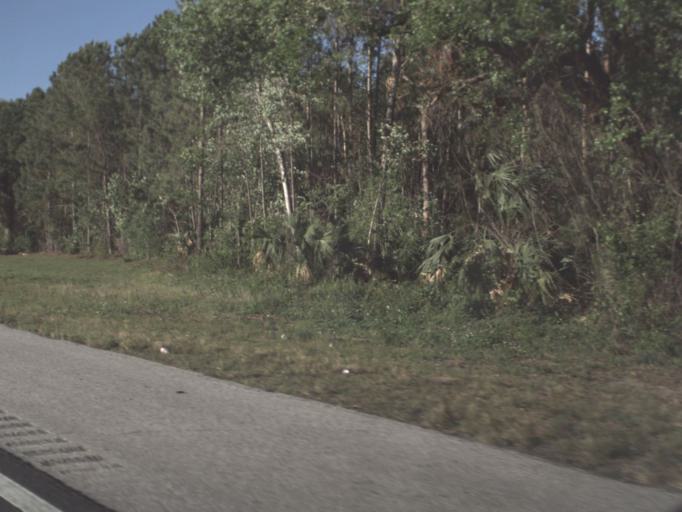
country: US
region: Florida
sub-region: Flagler County
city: Flagler Beach
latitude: 29.4906
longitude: -81.1892
